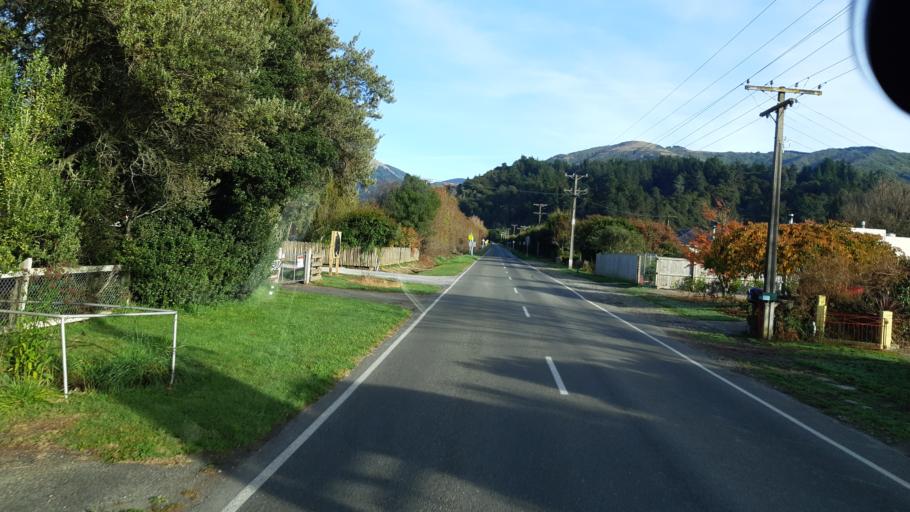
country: NZ
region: Tasman
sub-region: Tasman District
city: Motueka
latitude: -41.0960
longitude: 172.9715
